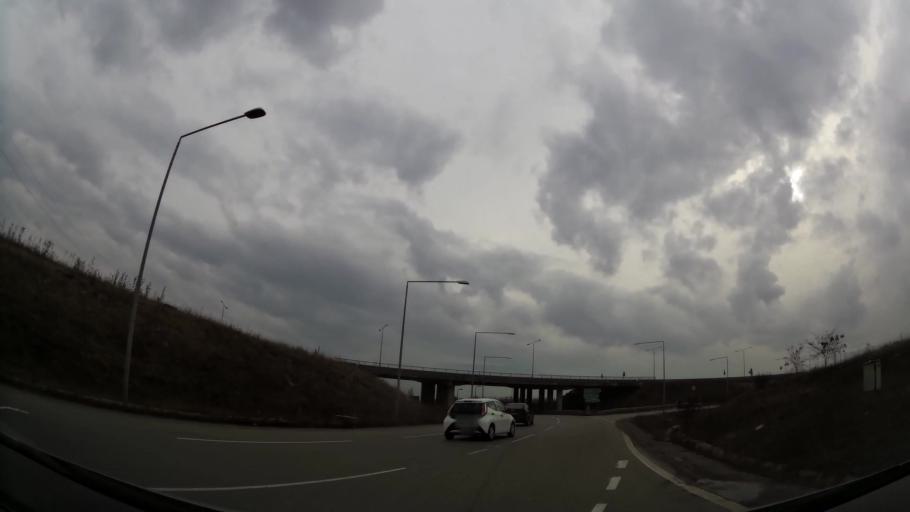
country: BG
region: Sofiya
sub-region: Obshtina Bozhurishte
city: Bozhurishte
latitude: 42.7131
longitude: 23.2289
